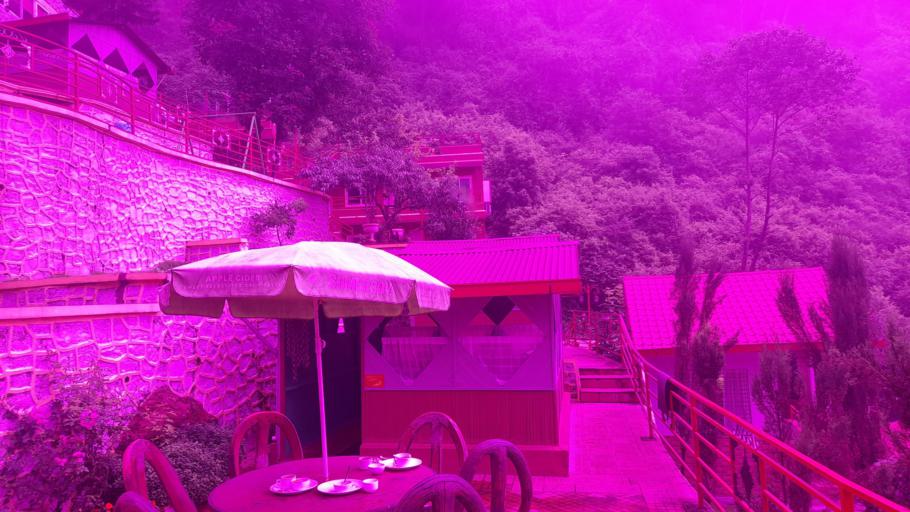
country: NP
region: Central Region
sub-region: Bagmati Zone
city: Kathmandu
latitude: 27.8058
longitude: 85.2743
